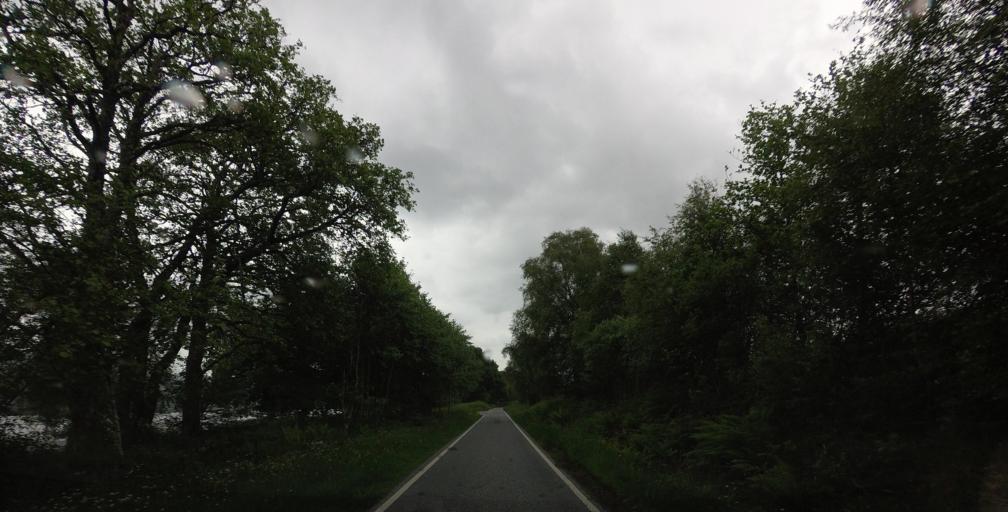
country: GB
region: Scotland
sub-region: Highland
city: Fort William
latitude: 56.8425
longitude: -5.2394
